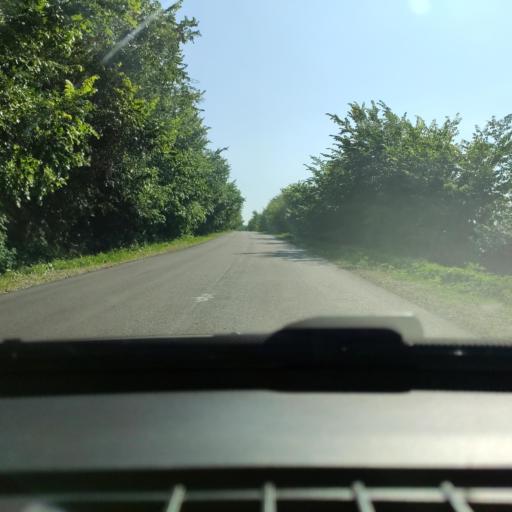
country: RU
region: Voronezj
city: Anna
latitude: 51.6333
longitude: 40.3551
